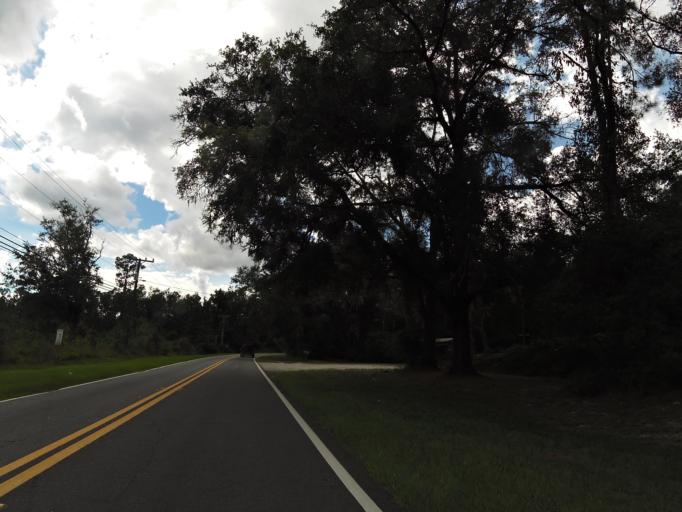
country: US
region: Florida
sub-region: Saint Johns County
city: Saint Augustine
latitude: 29.9058
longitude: -81.4929
